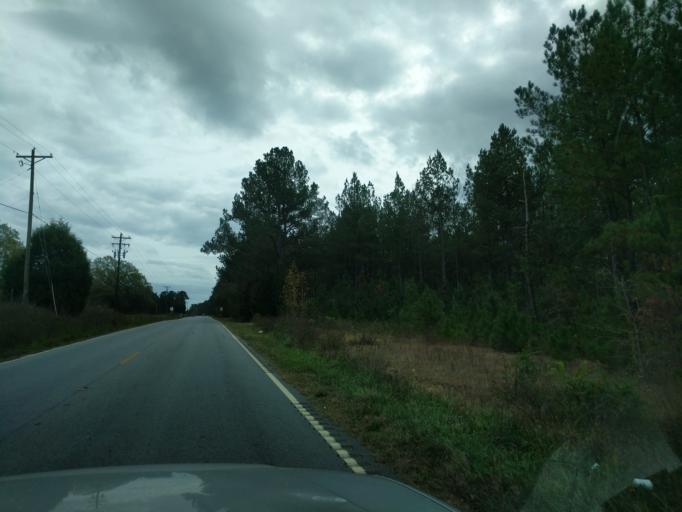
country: US
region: South Carolina
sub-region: Saluda County
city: Saluda
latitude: 34.0233
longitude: -81.7929
